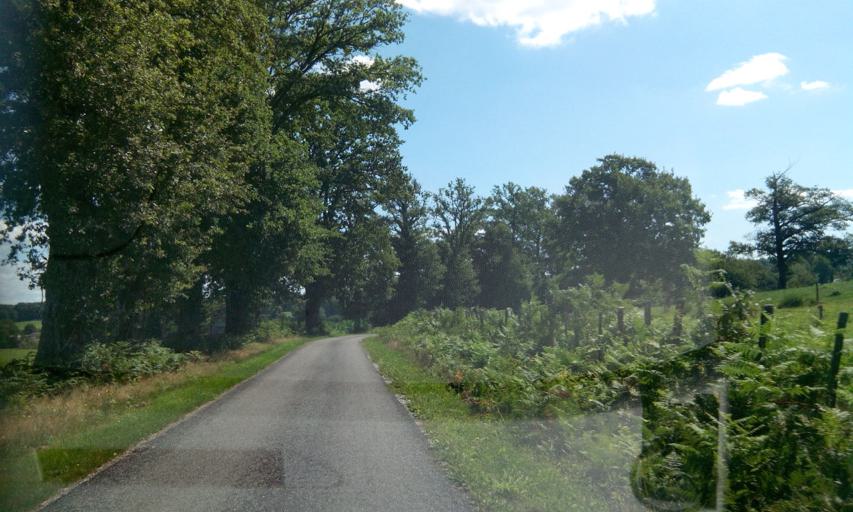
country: FR
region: Limousin
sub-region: Departement de la Haute-Vienne
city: Saint-Leonard-de-Noblat
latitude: 45.7990
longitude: 1.4668
